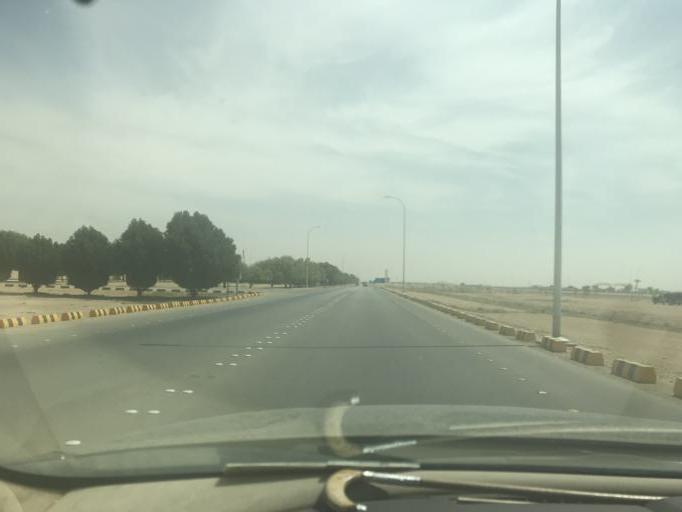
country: SA
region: Ar Riyad
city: Riyadh
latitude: 24.9824
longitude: 46.6844
